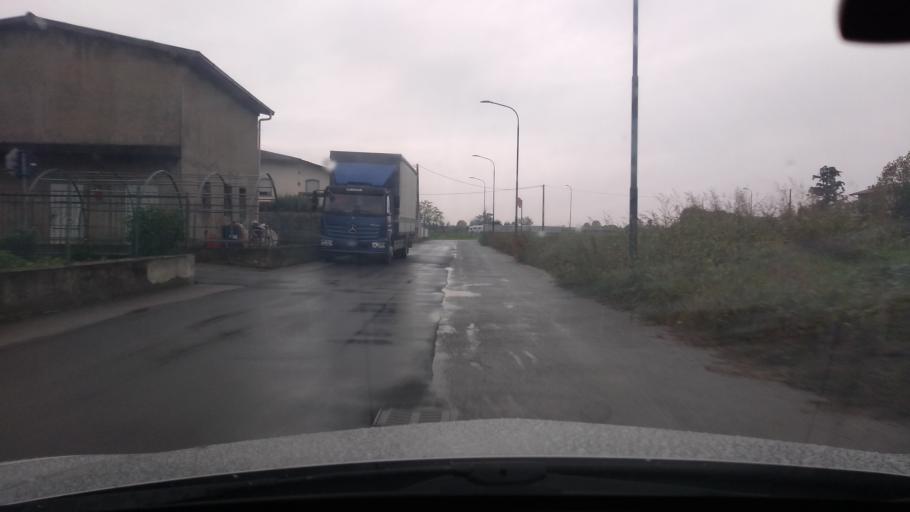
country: IT
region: Lombardy
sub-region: Provincia di Bergamo
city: Mornico al Serio
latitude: 45.5918
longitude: 9.8021
